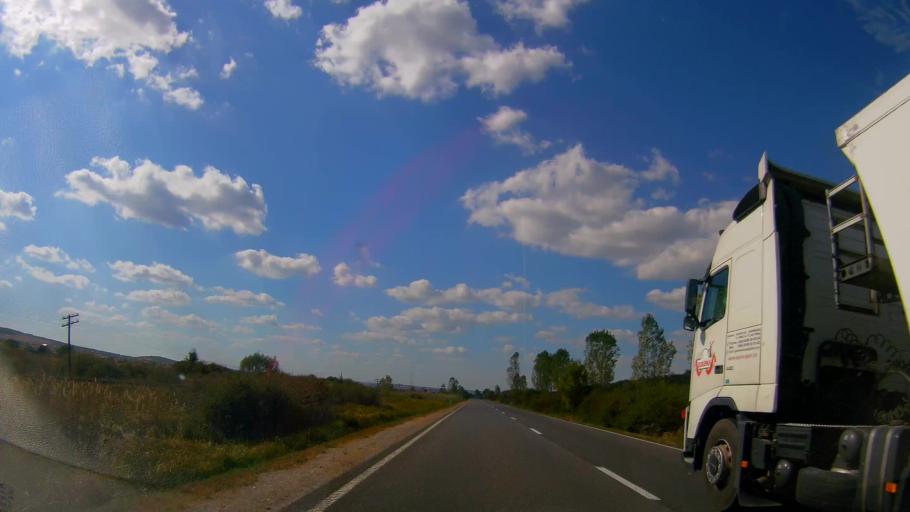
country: RO
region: Salaj
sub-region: Comuna Sarmasag
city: Sarmasag
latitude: 47.3261
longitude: 22.8751
